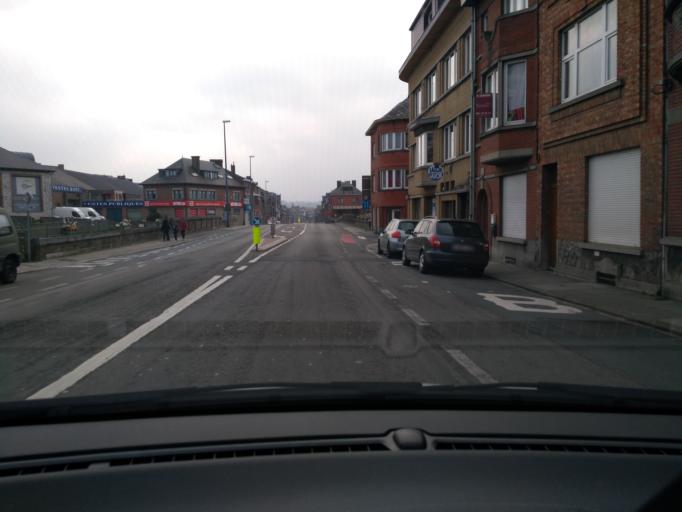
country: BE
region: Wallonia
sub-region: Province de Namur
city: Namur
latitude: 50.4724
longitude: 4.8386
